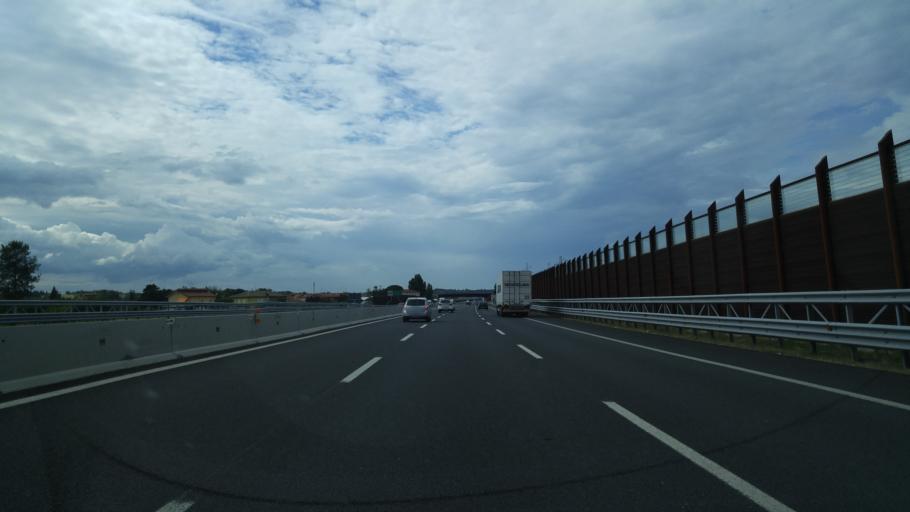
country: IT
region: Emilia-Romagna
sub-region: Provincia di Rimini
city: Coriano
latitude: 44.0024
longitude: 12.6046
